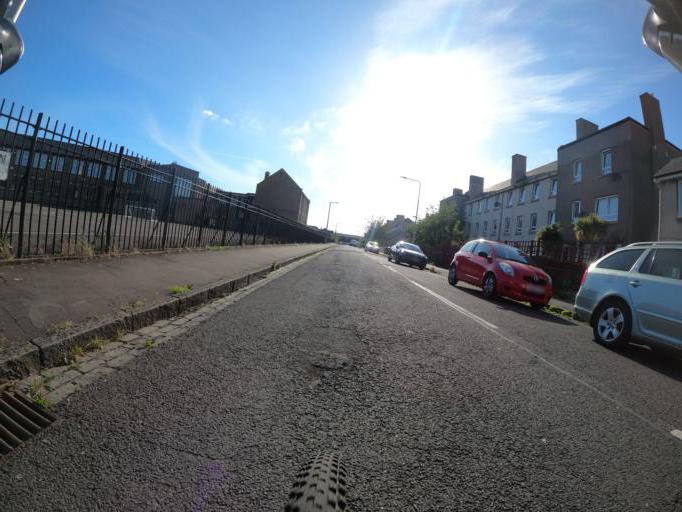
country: GB
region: Scotland
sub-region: Edinburgh
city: Edinburgh
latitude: 55.9770
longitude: -3.2253
